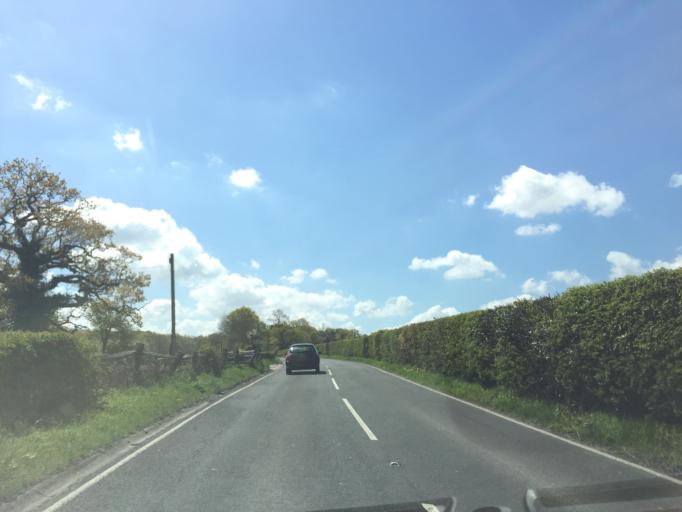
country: GB
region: England
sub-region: Kent
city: Edenbridge
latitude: 51.1379
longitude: 0.1077
